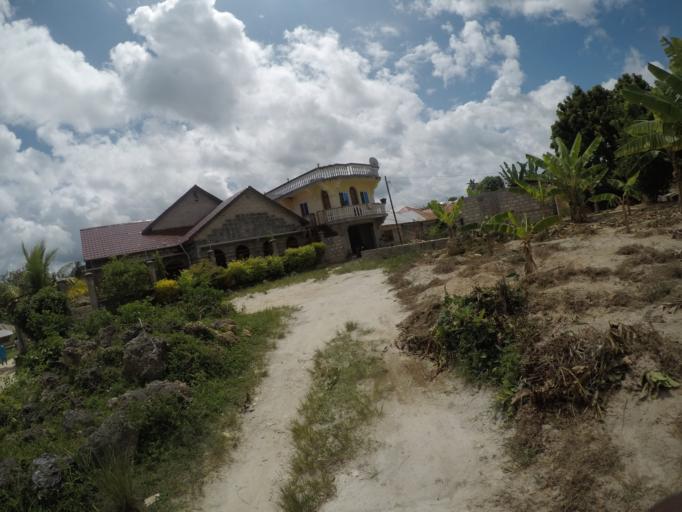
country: TZ
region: Pemba South
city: Chake Chake
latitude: -5.2304
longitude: 39.7822
